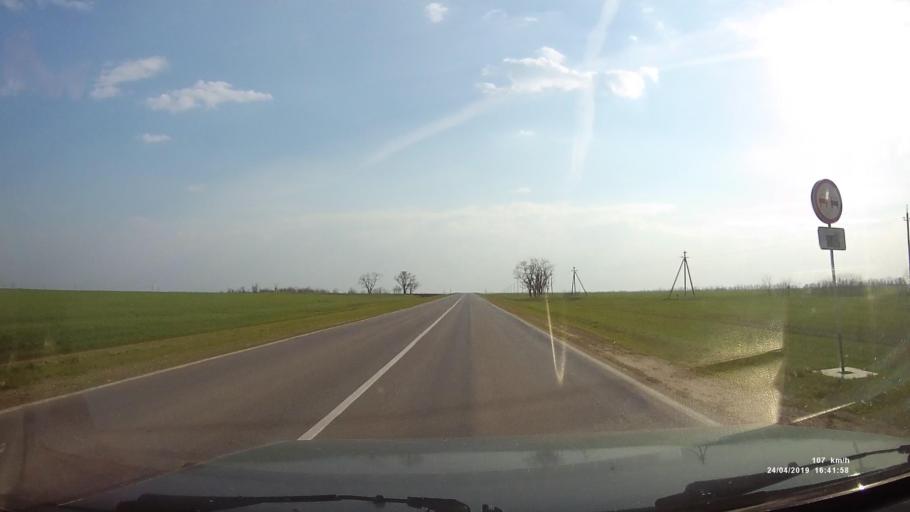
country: RU
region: Rostov
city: Gundorovskiy
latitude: 46.8135
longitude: 41.8605
